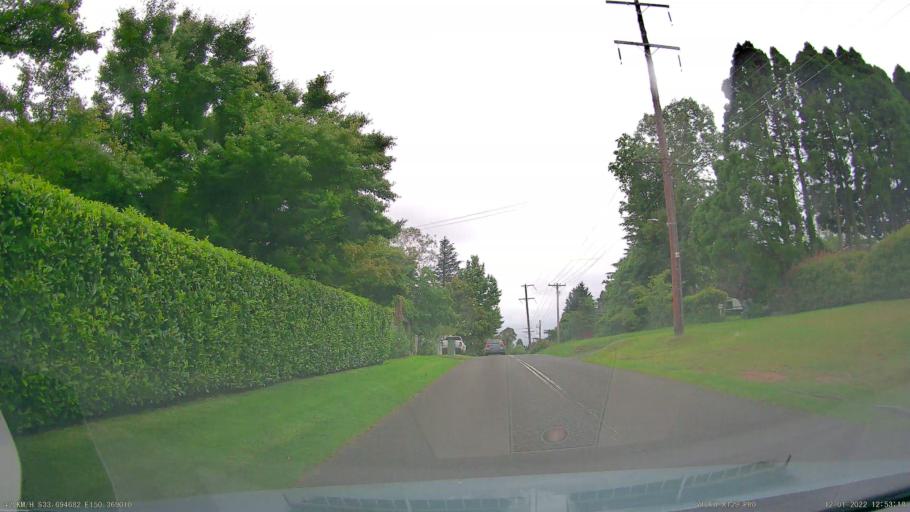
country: AU
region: New South Wales
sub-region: Blue Mountains Municipality
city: Leura
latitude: -33.6945
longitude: 150.3688
